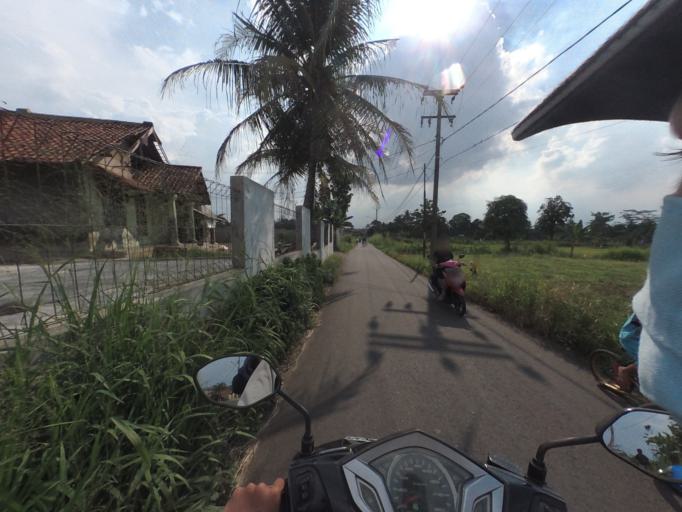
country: ID
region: West Java
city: Ciampea
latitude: -6.6045
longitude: 106.7045
